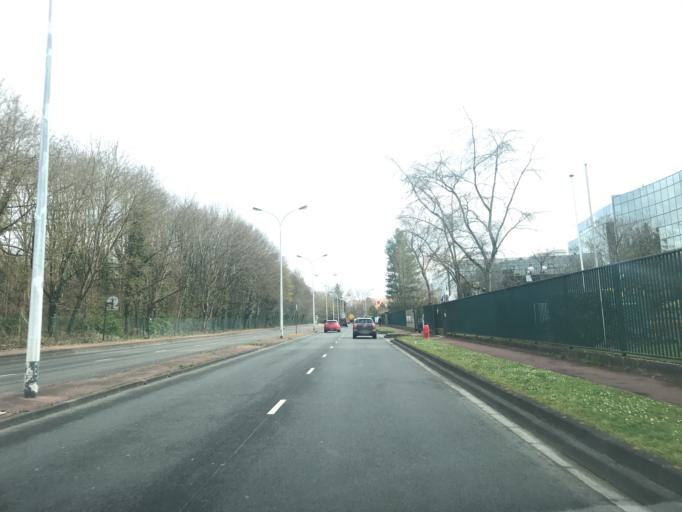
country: FR
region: Ile-de-France
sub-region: Departement des Yvelines
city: Velizy-Villacoublay
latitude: 48.7845
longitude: 2.2069
